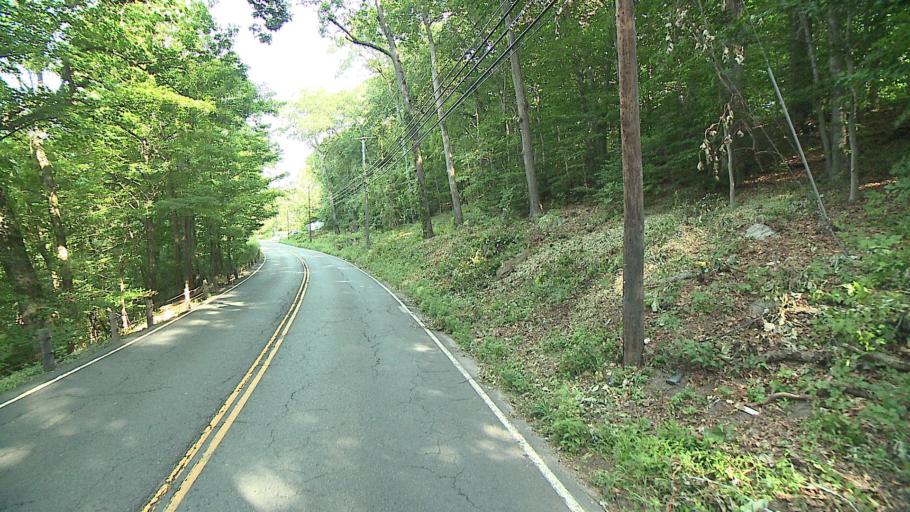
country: US
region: Connecticut
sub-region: Fairfield County
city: Danbury
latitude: 41.4225
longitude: -73.4694
